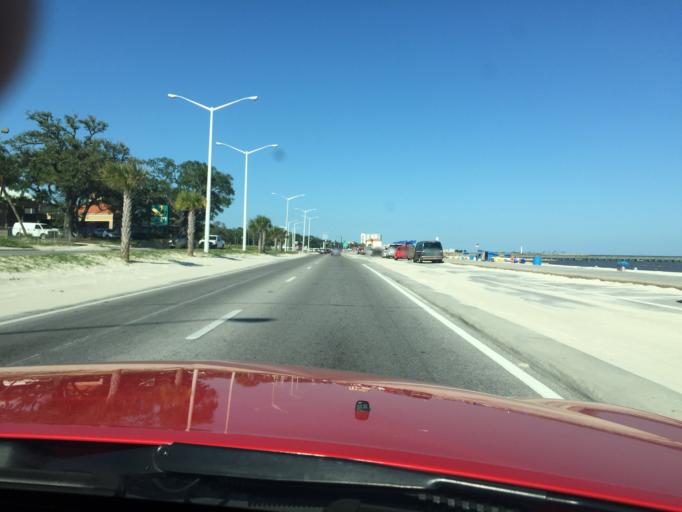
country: US
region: Mississippi
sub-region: Harrison County
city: Biloxi
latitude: 30.3903
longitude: -88.9786
